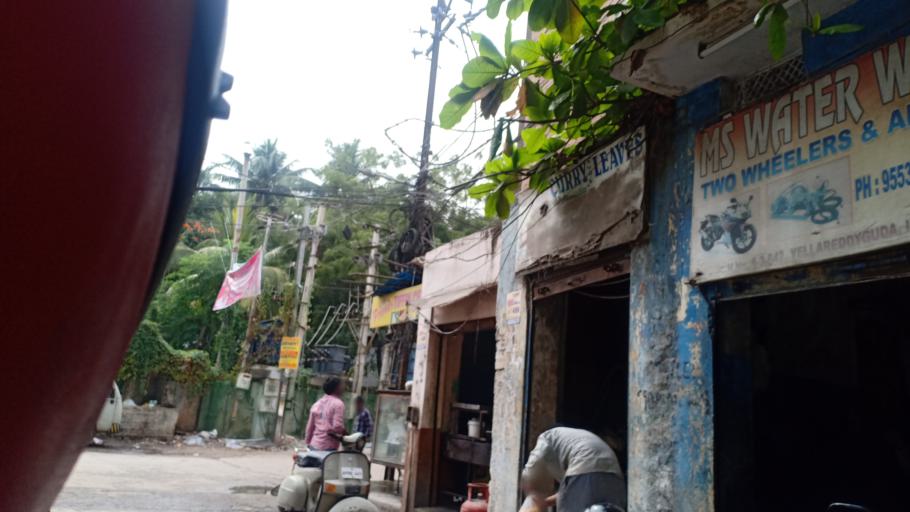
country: IN
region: Telangana
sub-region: Hyderabad
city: Hyderabad
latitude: 17.4335
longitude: 78.4397
